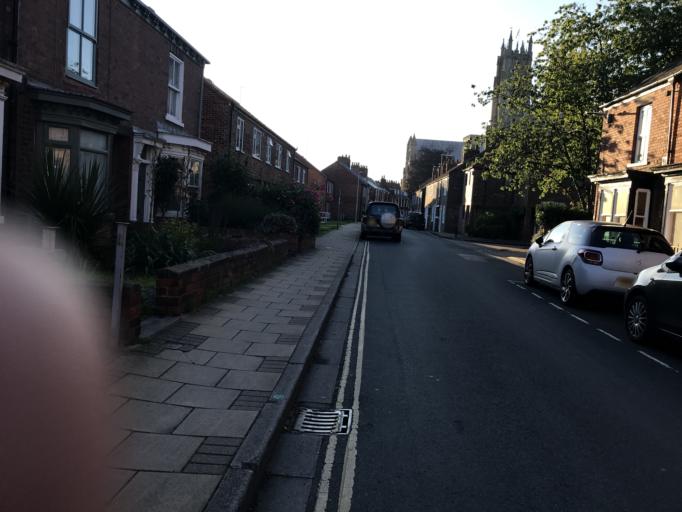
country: GB
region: England
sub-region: East Riding of Yorkshire
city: Beverley
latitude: 53.8393
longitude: -0.4281
